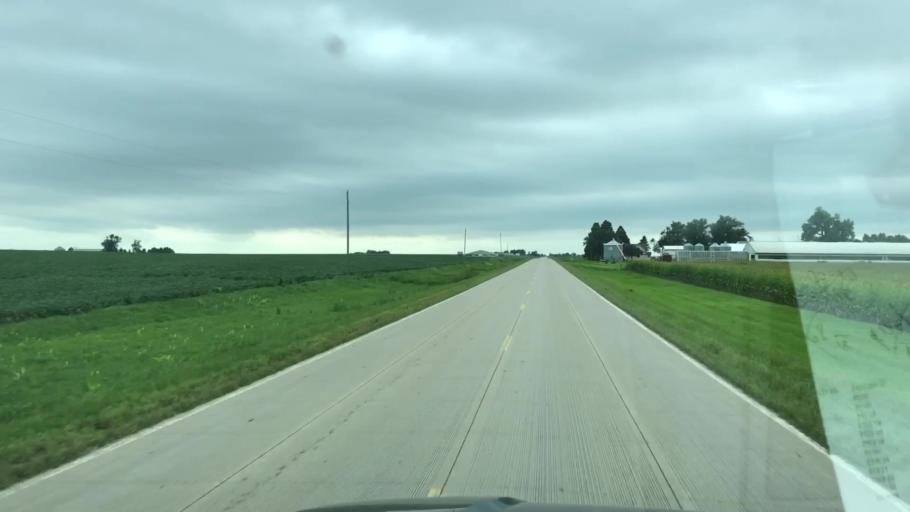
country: US
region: Iowa
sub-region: O'Brien County
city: Sheldon
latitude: 43.1351
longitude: -95.9792
